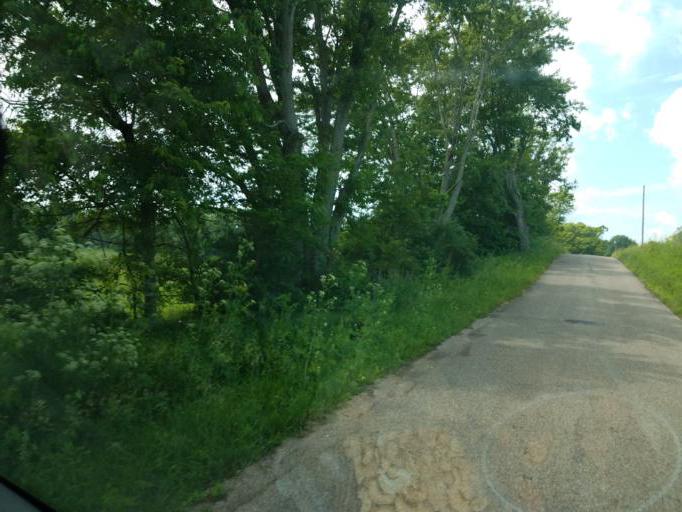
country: US
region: Ohio
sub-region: Knox County
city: Fredericktown
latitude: 40.4708
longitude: -82.5694
